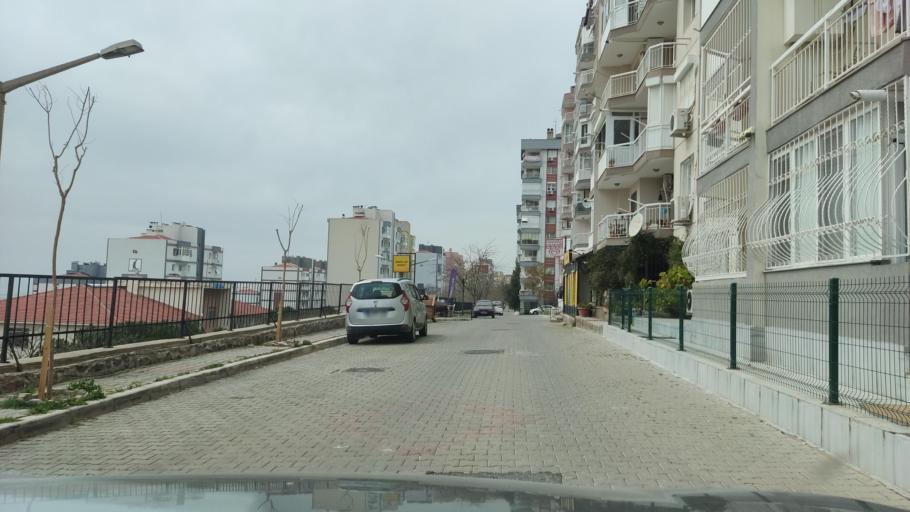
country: TR
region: Izmir
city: Karsiyaka
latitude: 38.5038
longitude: 27.0758
